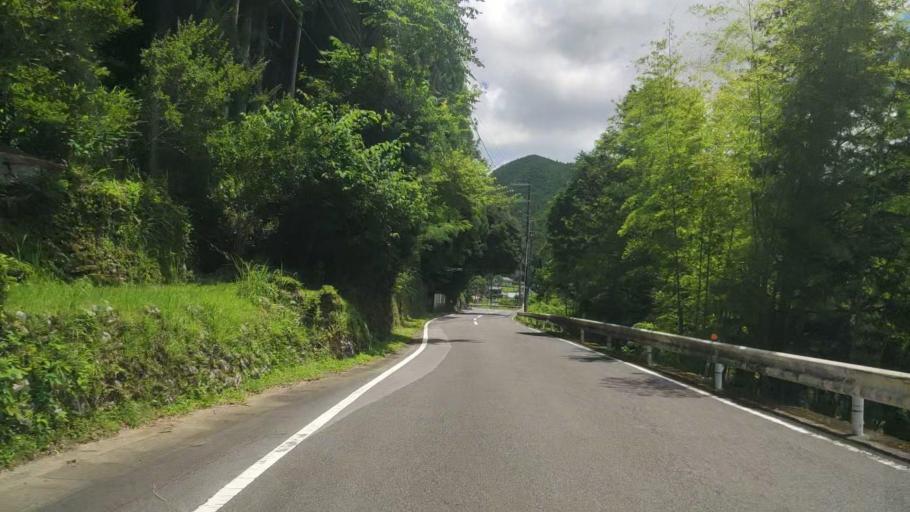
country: JP
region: Mie
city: Owase
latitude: 33.9586
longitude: 136.0659
